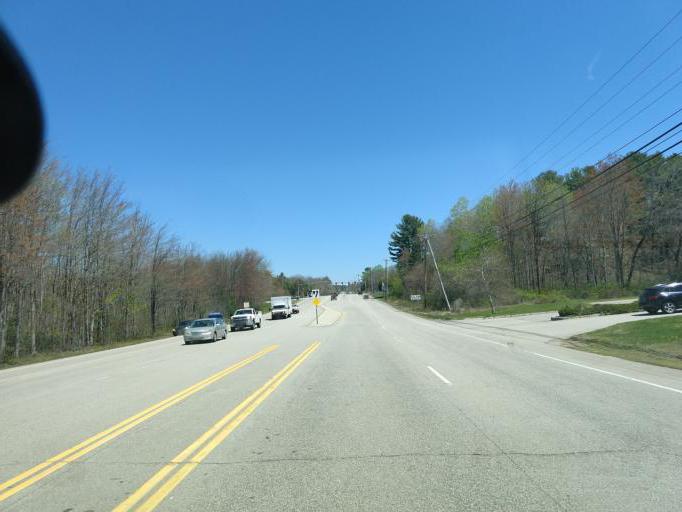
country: US
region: Maine
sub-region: York County
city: York Harbor
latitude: 43.1531
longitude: -70.6611
